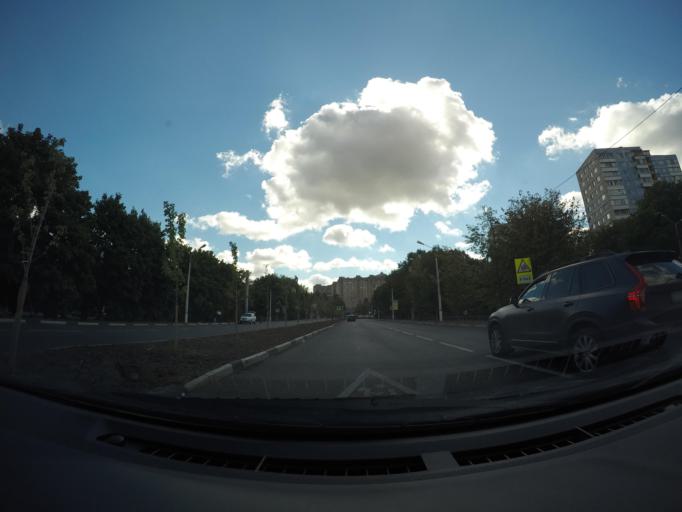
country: RU
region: Moskovskaya
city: Ramenskoye
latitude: 55.5841
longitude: 38.2069
